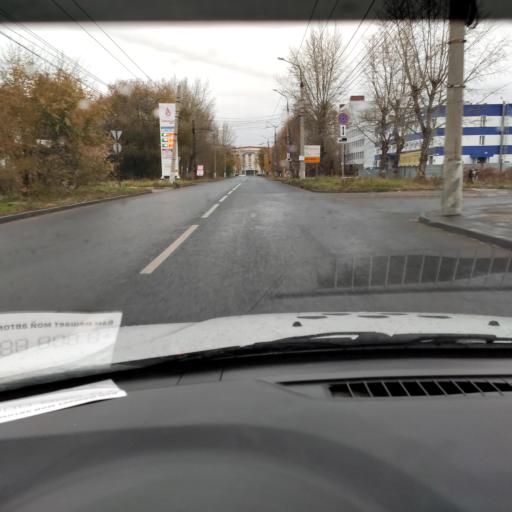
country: RU
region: Samara
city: Tol'yatti
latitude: 53.5160
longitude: 49.4561
